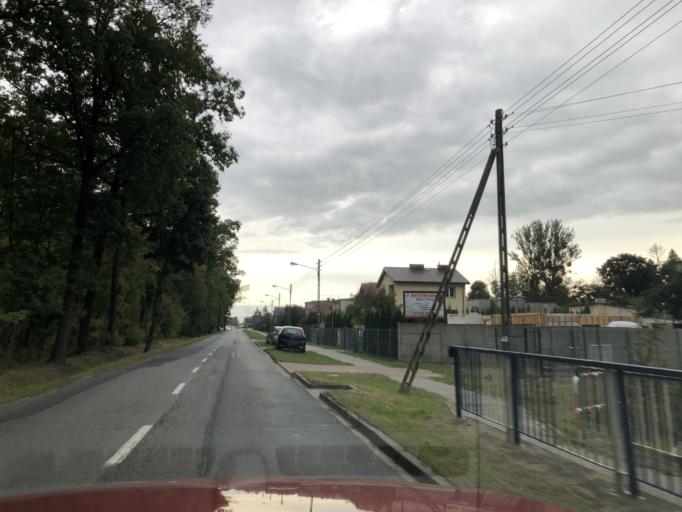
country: PL
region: Lower Silesian Voivodeship
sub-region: Powiat wroclawski
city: Dlugoleka
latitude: 51.1816
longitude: 17.1894
